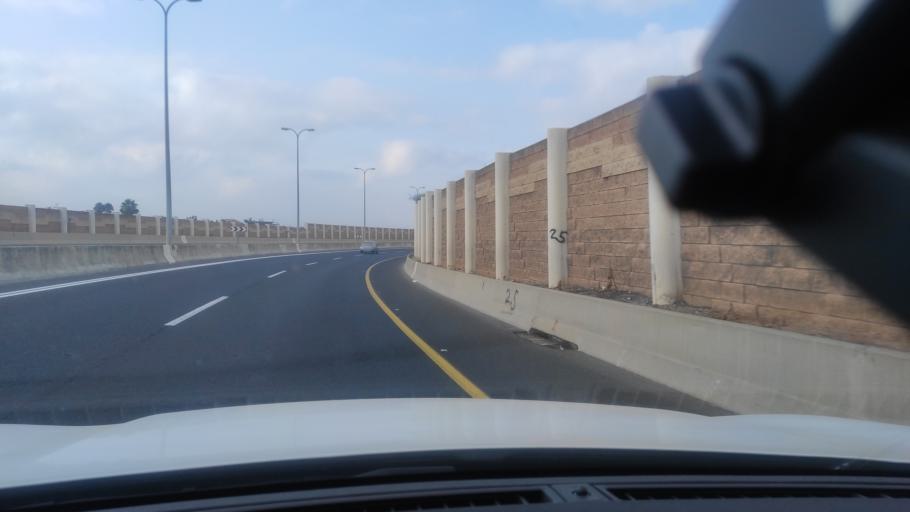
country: IL
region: Central District
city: Kfar Saba
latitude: 32.1589
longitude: 34.9263
